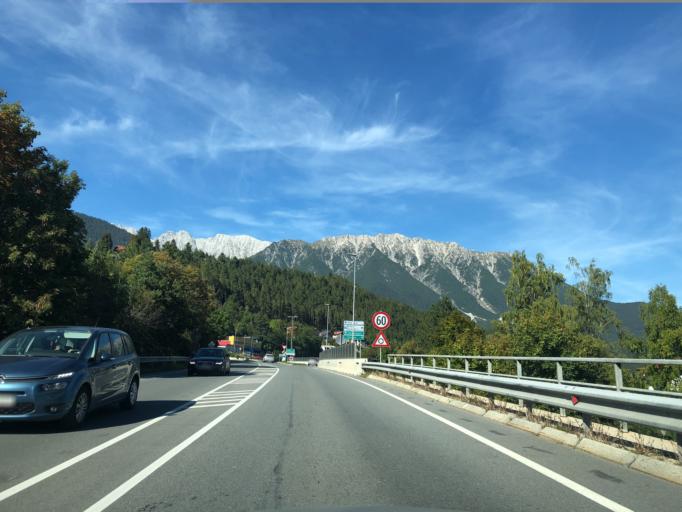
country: AT
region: Tyrol
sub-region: Politischer Bezirk Imst
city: Imst
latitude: 47.2464
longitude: 10.7452
